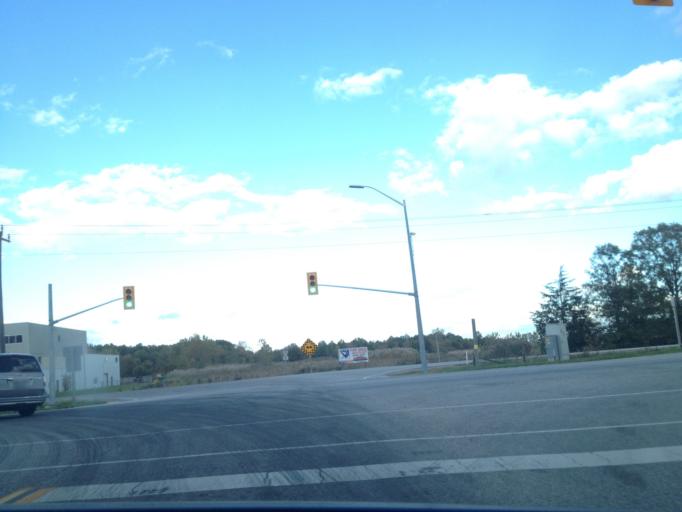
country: CA
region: Ontario
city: Amherstburg
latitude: 42.0984
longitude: -82.7333
